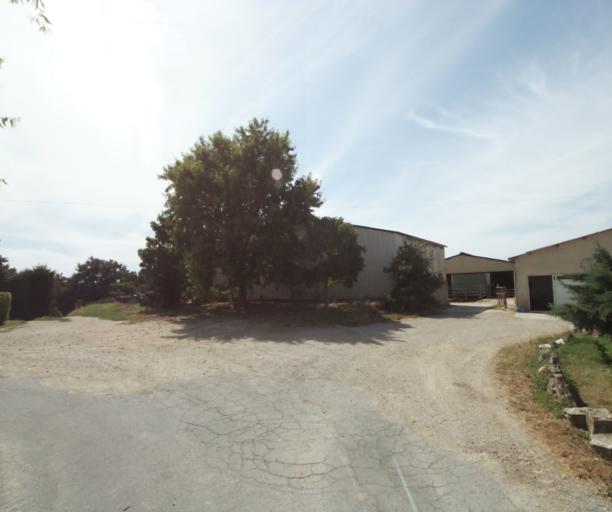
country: FR
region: Midi-Pyrenees
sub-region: Departement du Tarn
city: Soreze
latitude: 43.5081
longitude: 2.0722
